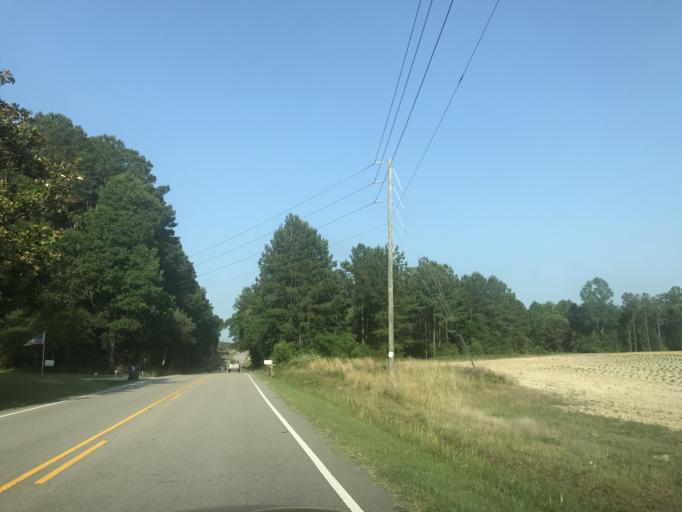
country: US
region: North Carolina
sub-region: Wake County
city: Rolesville
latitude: 35.8614
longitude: -78.4781
